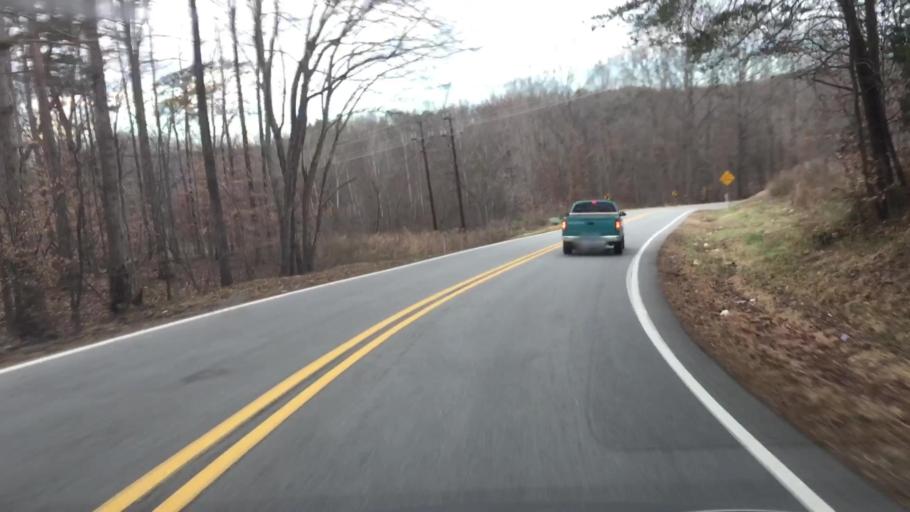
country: US
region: North Carolina
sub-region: Rockingham County
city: Reidsville
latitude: 36.3943
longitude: -79.6586
